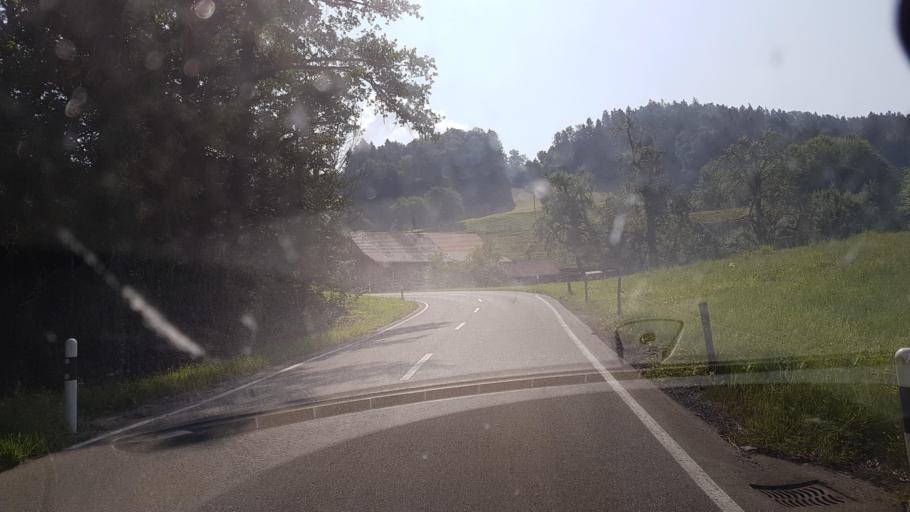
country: CH
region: Saint Gallen
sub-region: Wahlkreis Toggenburg
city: Mogelsberg
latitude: 47.3551
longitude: 9.1332
